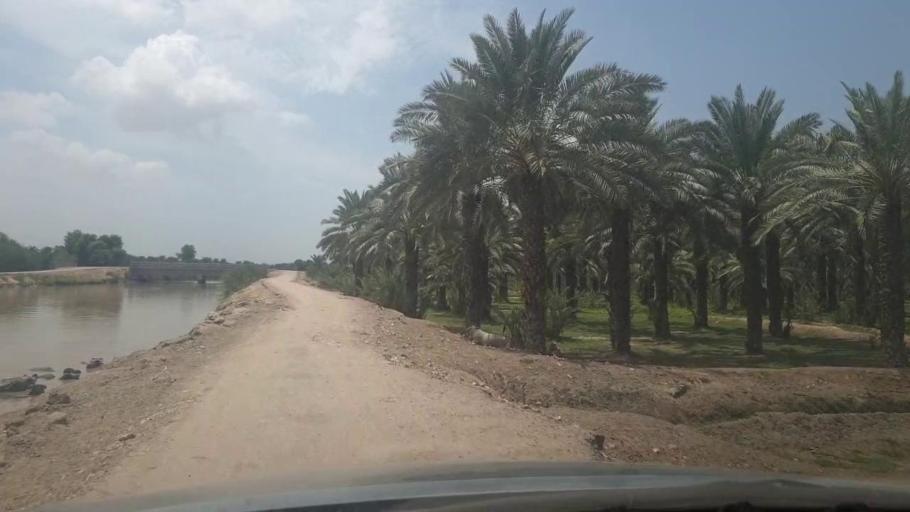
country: PK
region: Sindh
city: Kot Diji
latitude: 27.3960
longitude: 68.7607
